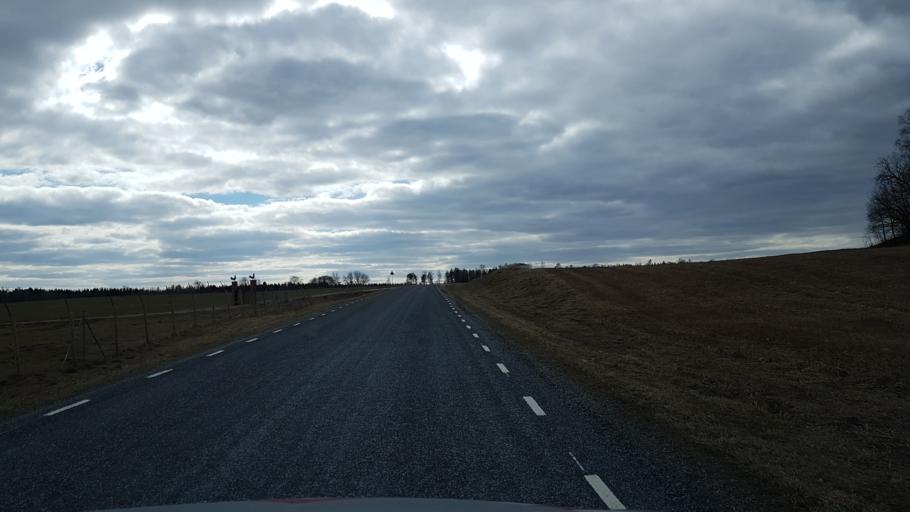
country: EE
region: Laeaene-Virumaa
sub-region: Tamsalu vald
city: Tamsalu
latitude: 59.2073
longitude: 26.1447
